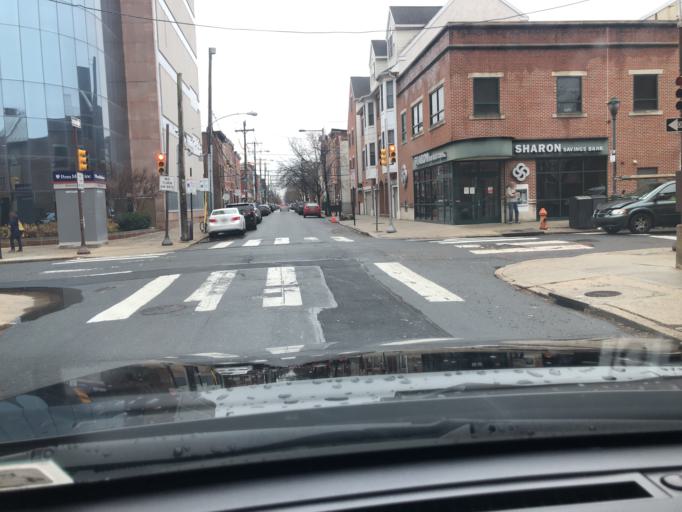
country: US
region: Pennsylvania
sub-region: Philadelphia County
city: Philadelphia
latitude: 39.9448
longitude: -75.1734
